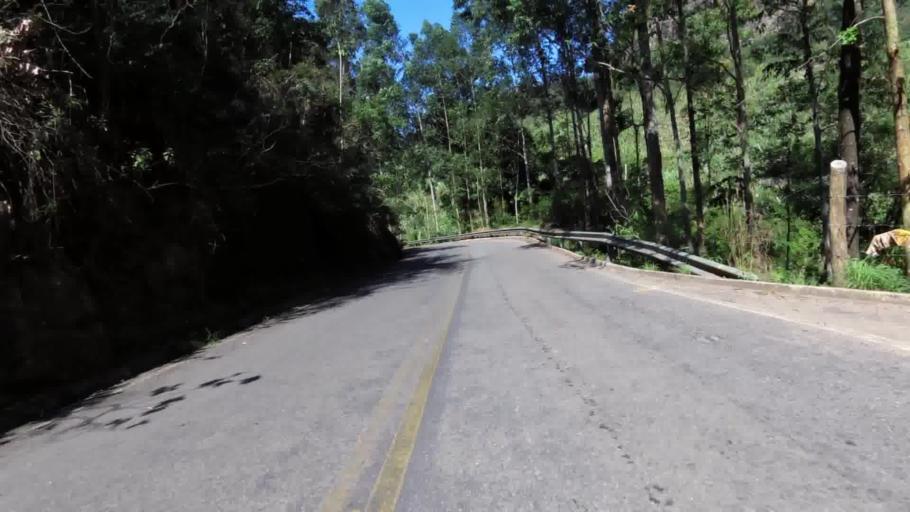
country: BR
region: Espirito Santo
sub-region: Alfredo Chaves
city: Alfredo Chaves
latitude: -20.5769
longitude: -40.8041
